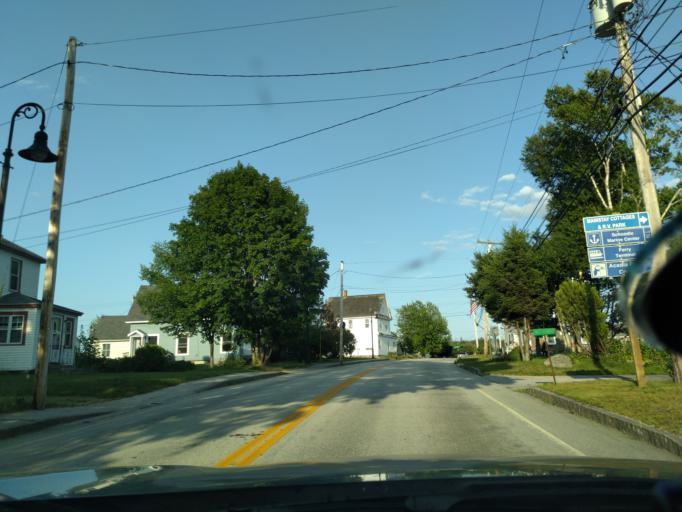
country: US
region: Maine
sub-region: Hancock County
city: Gouldsboro
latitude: 44.3956
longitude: -68.0810
